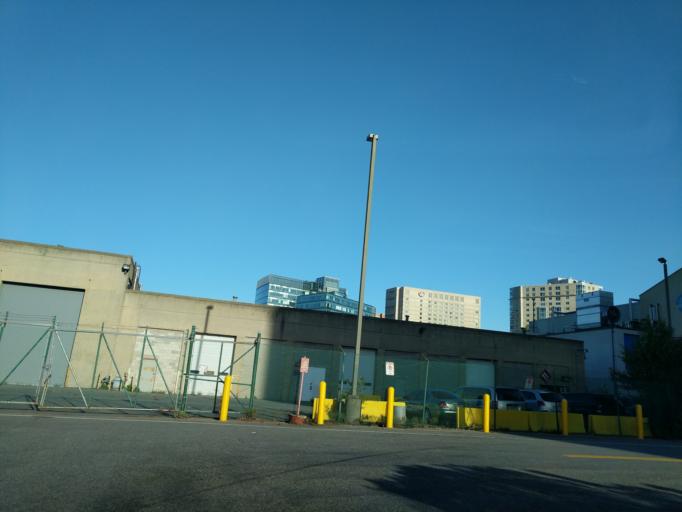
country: US
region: Massachusetts
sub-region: Suffolk County
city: South Boston
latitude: 42.3452
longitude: -71.0375
